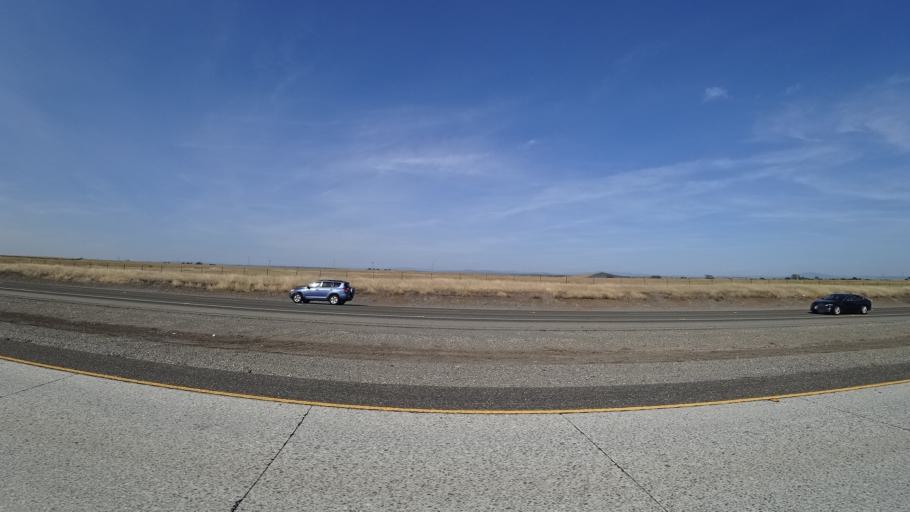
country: US
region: California
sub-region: Butte County
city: Durham
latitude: 39.6703
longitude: -121.7501
